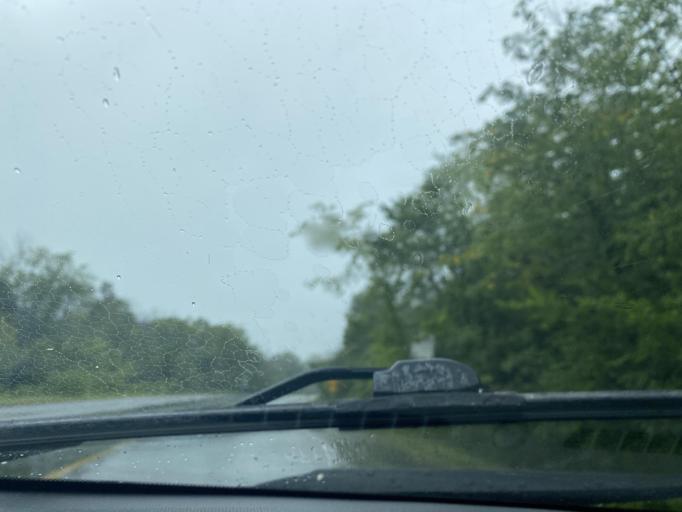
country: CA
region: Quebec
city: Baie-D'Urfe
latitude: 45.4390
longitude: -73.9081
